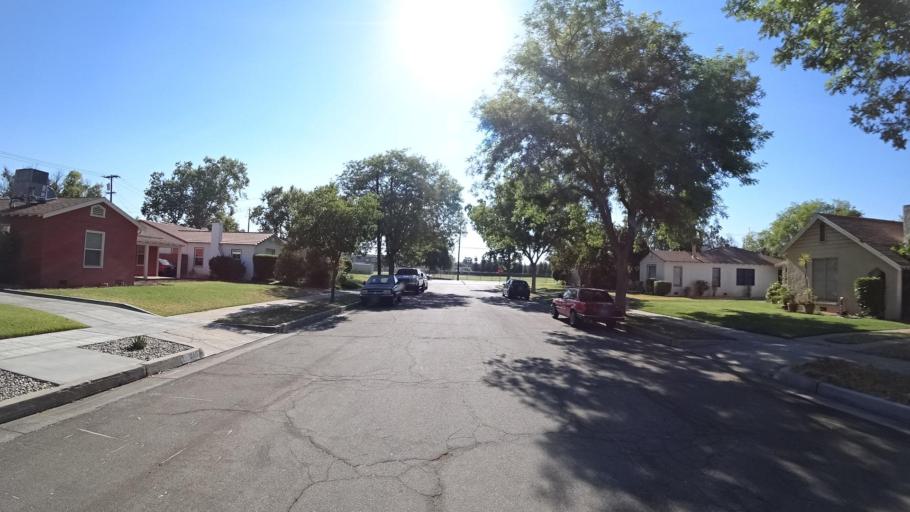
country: US
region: California
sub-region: Fresno County
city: Fresno
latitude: 36.7658
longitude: -119.8093
